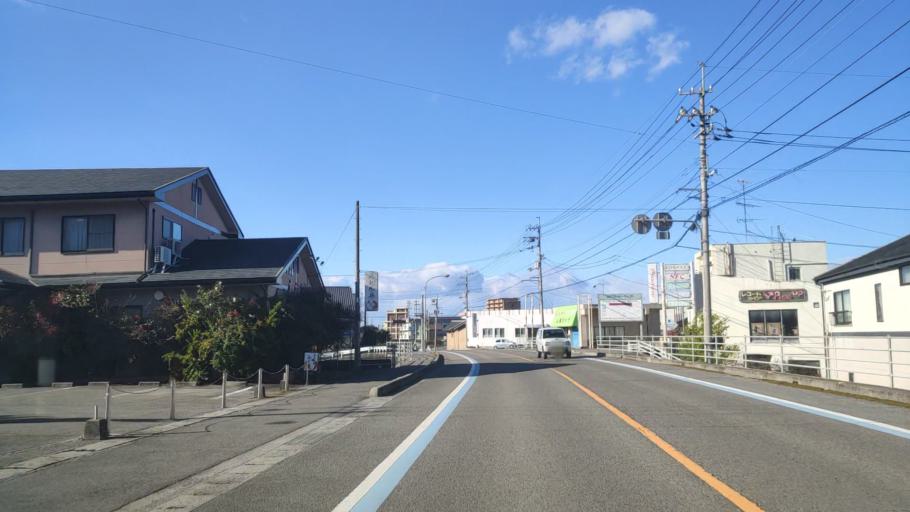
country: JP
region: Ehime
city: Saijo
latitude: 33.9079
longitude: 133.1843
